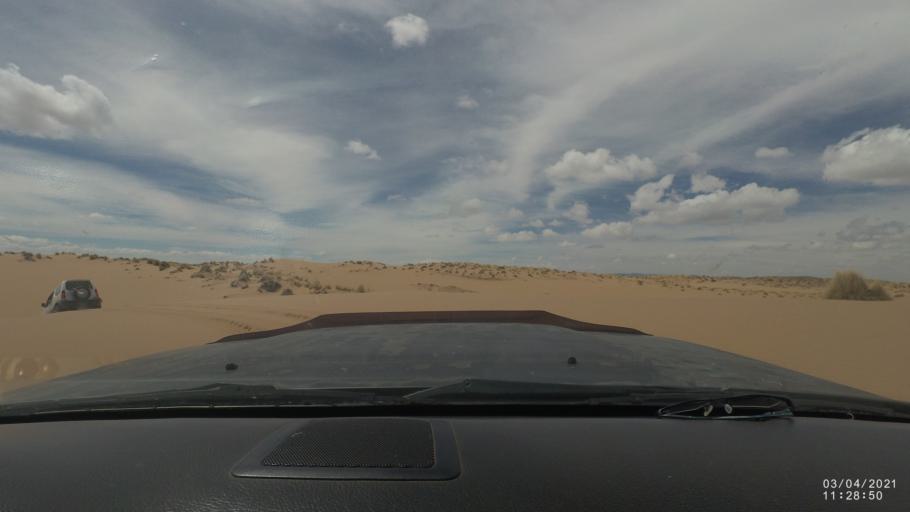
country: BO
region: Oruro
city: Poopo
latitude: -18.7030
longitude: -67.5097
